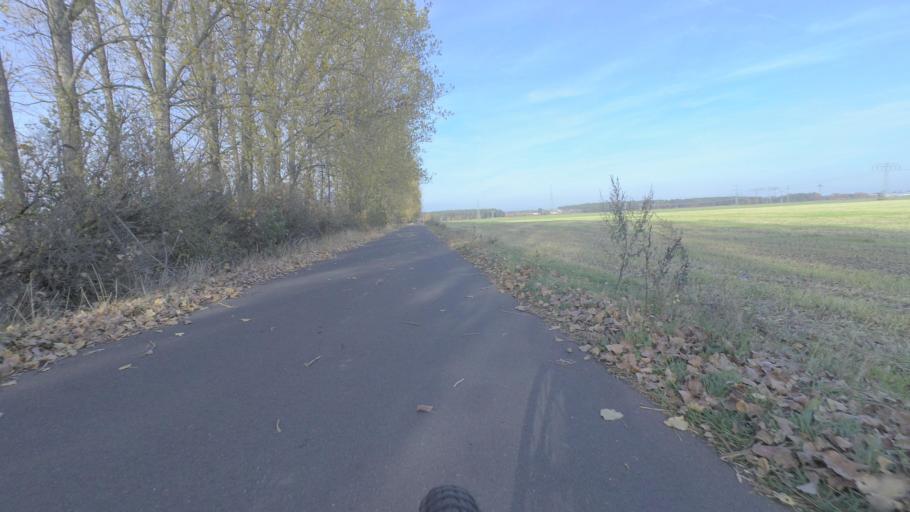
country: DE
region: Brandenburg
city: Trebbin
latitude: 52.2208
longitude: 13.2897
